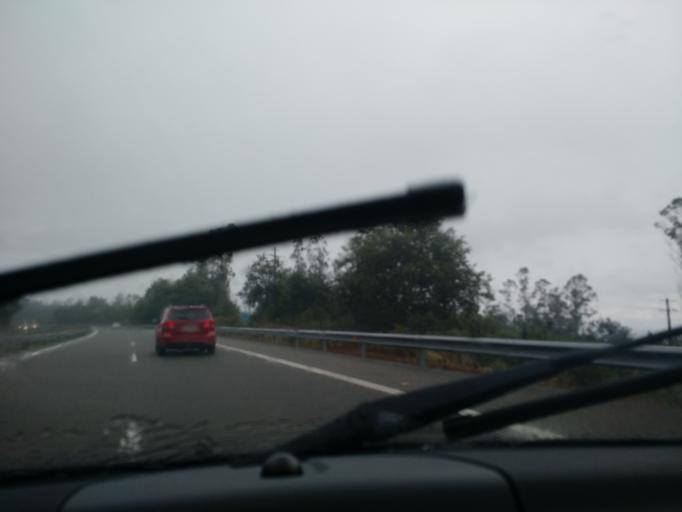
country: ES
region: Galicia
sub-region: Provincia da Coruna
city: Mesia
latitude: 43.1503
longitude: -8.3278
